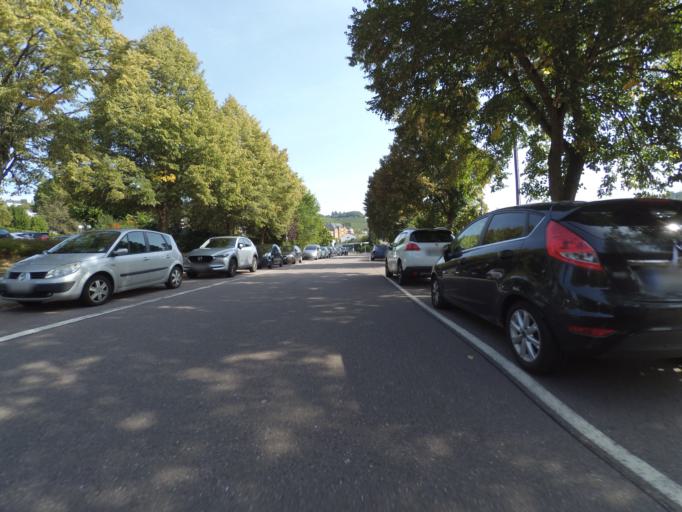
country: DE
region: Rheinland-Pfalz
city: Saarburg
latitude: 49.6033
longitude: 6.5393
